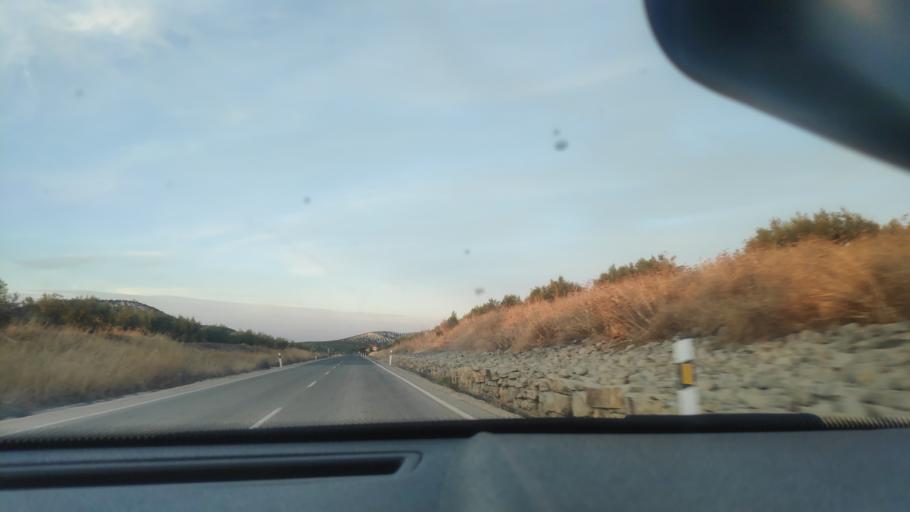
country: ES
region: Andalusia
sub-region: Provincia de Jaen
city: Escanuela
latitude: 37.8607
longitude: -4.0421
